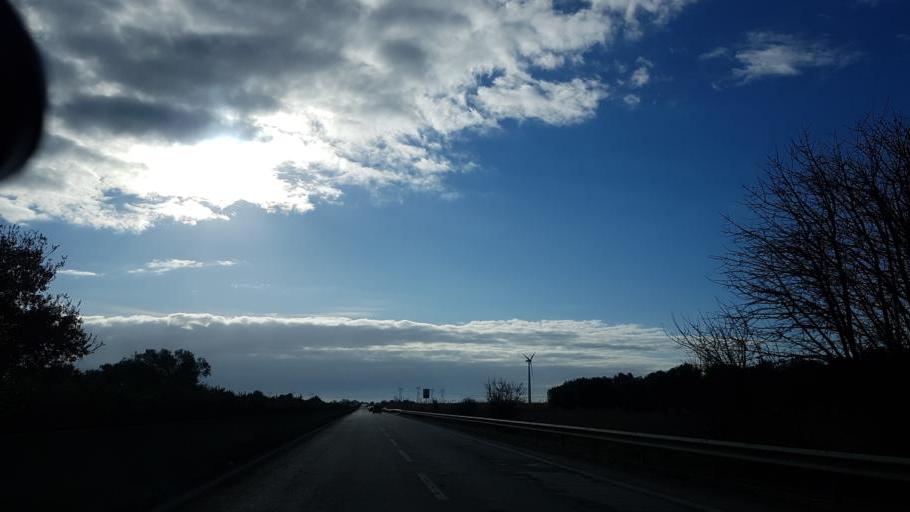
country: IT
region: Apulia
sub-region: Provincia di Brindisi
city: La Rosa
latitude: 40.5750
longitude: 17.9814
